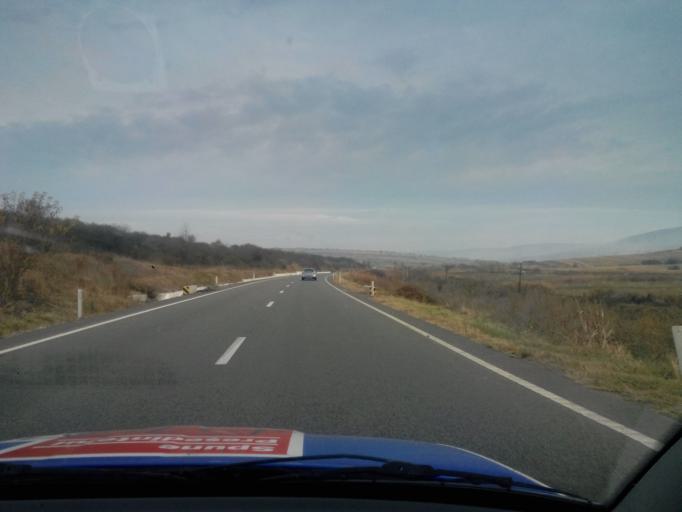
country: RO
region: Vaslui
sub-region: Comuna Oltenesti
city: Oltenesti
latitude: 46.5837
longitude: 27.8694
